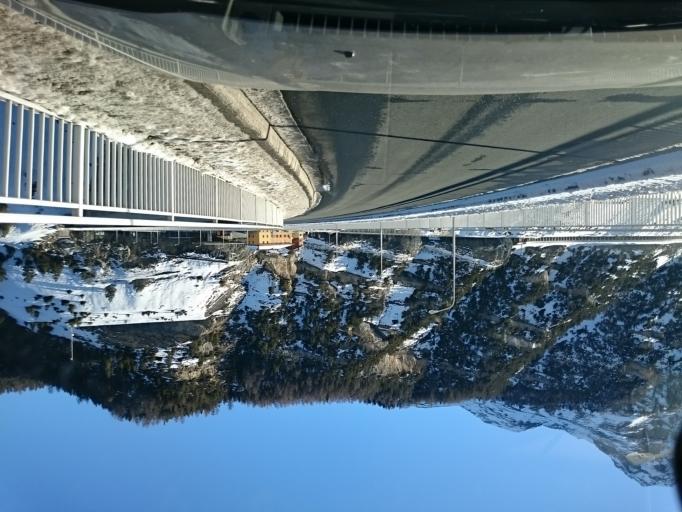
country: IT
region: Lombardy
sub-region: Provincia di Sondrio
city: Livigno
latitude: 46.6234
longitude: 10.1932
